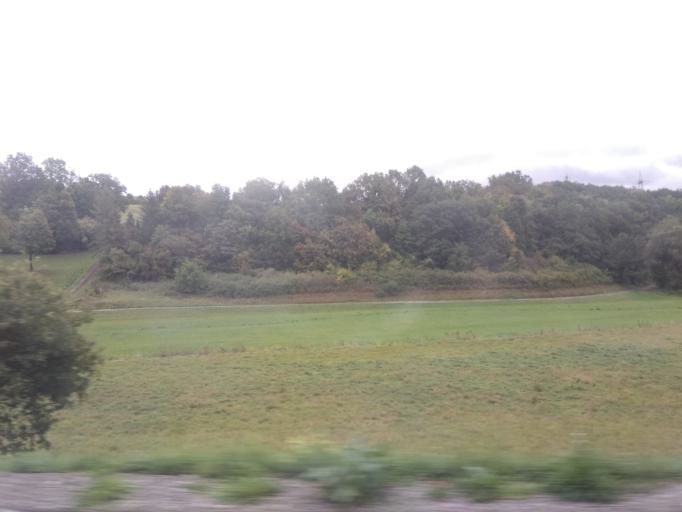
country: DE
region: Baden-Wuerttemberg
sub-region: Karlsruhe Region
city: Billigheim
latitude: 49.3540
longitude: 9.2760
